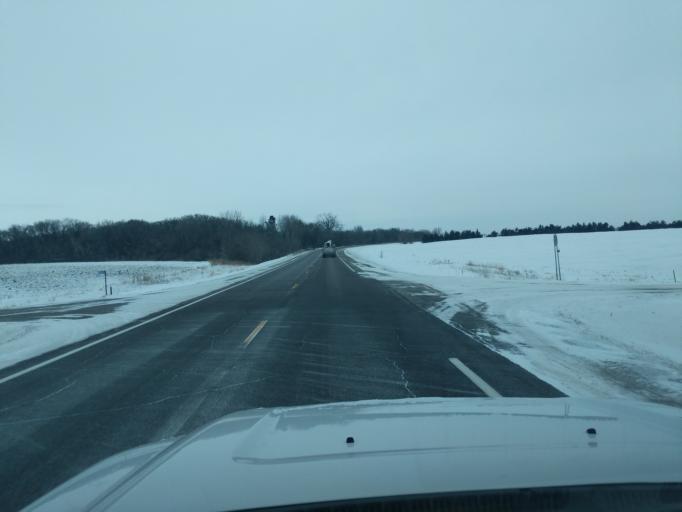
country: US
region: Minnesota
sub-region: Redwood County
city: Redwood Falls
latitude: 44.5710
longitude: -94.9946
